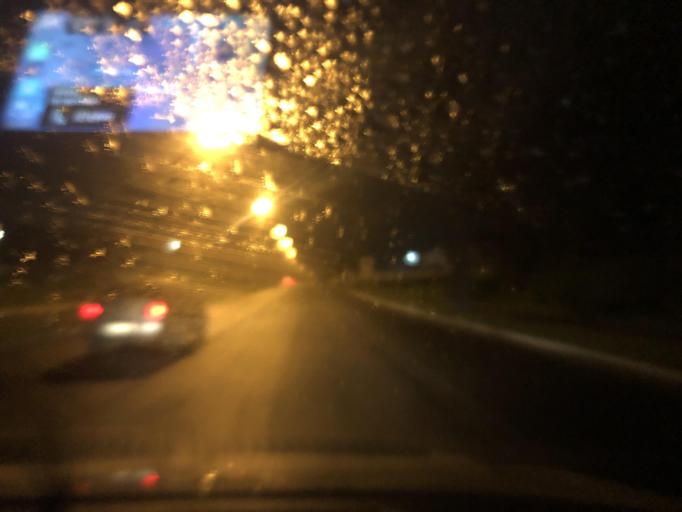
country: BR
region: Santa Catarina
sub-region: Joinville
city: Joinville
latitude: -26.3757
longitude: -48.8393
